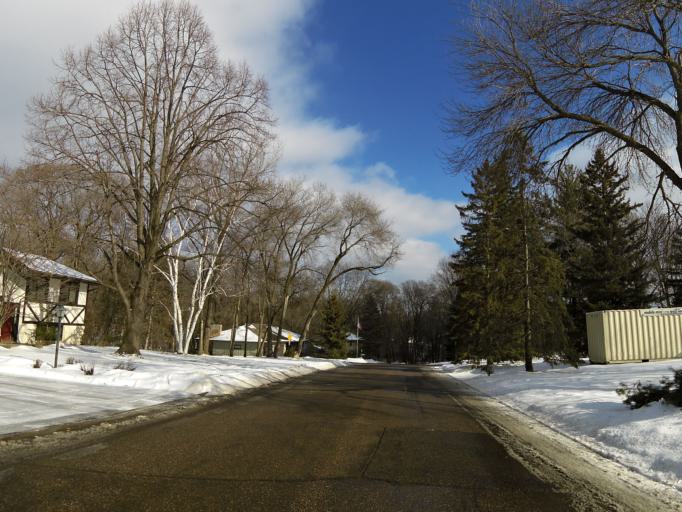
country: US
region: Minnesota
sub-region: Hennepin County
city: Hopkins
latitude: 44.9135
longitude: -93.4660
